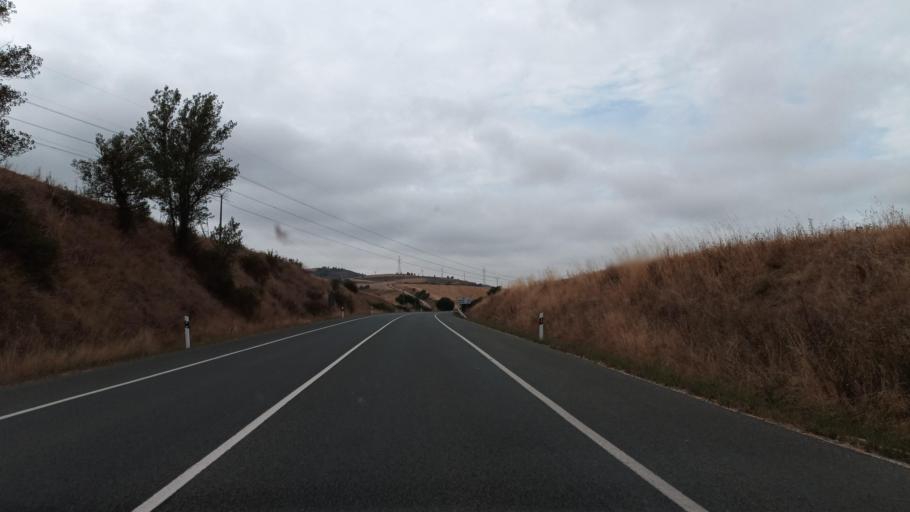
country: ES
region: Castille and Leon
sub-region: Provincia de Burgos
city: Castil de Peones
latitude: 42.4842
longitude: -3.3811
